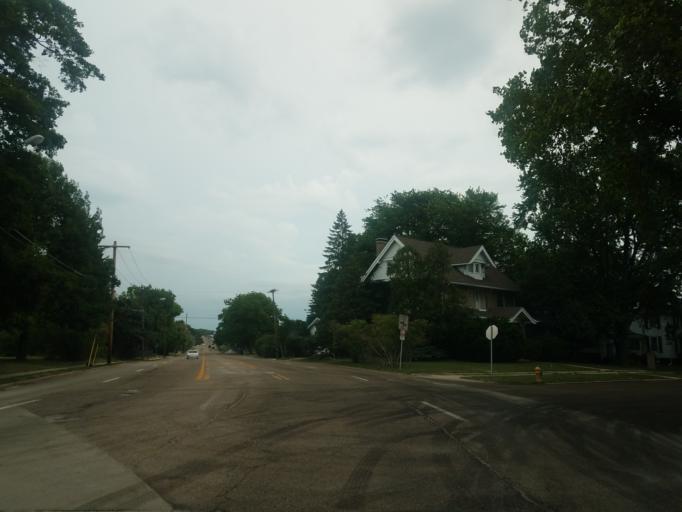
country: US
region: Illinois
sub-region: McLean County
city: Bloomington
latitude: 40.4807
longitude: -88.9748
